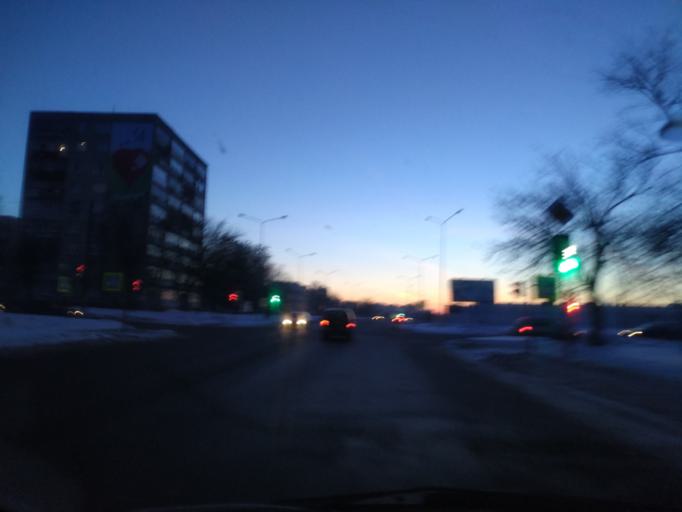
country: BY
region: Mogilev
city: Mahilyow
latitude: 53.8812
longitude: 30.3219
